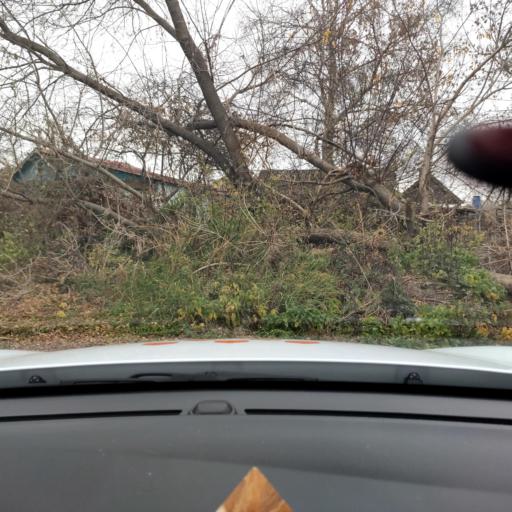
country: RU
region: Tatarstan
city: Vysokaya Gora
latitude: 55.8738
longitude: 49.2531
